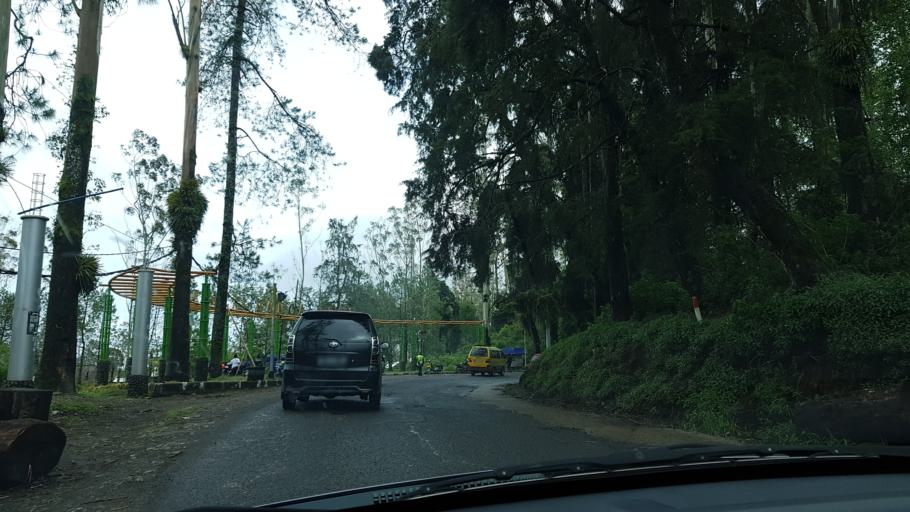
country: ID
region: West Java
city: Banjar
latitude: -7.1413
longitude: 107.3953
